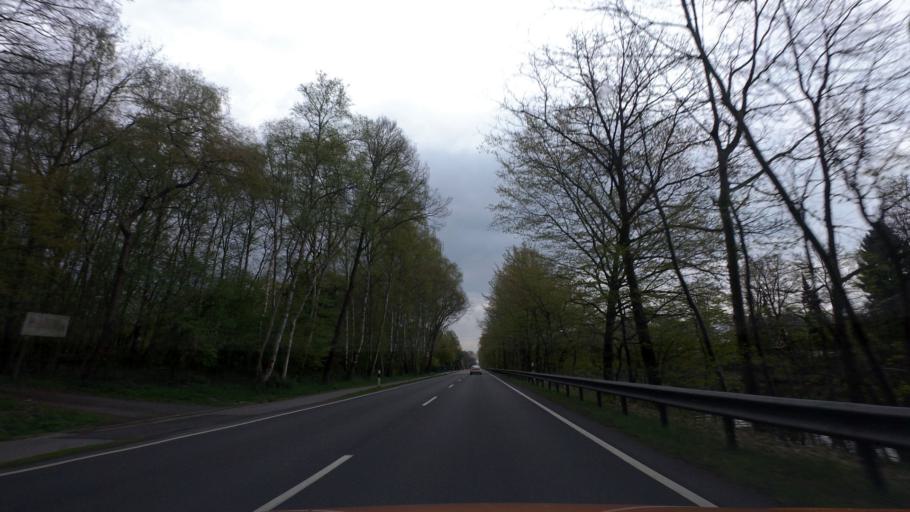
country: DE
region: Lower Saxony
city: Wardenburg
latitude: 53.1082
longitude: 8.1389
